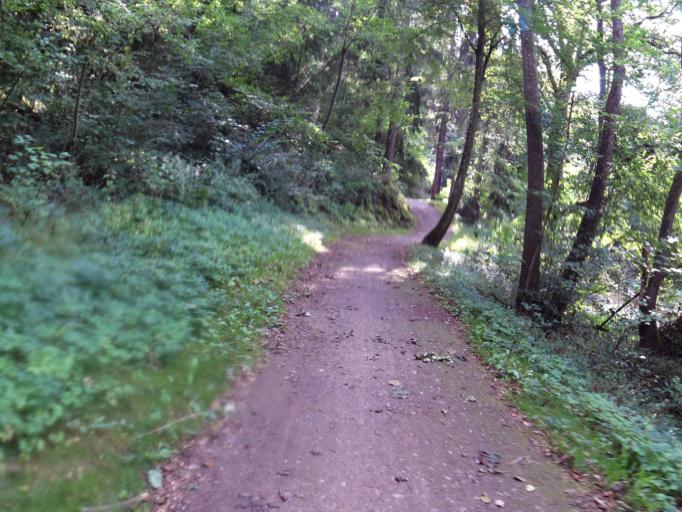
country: DE
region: Rheinland-Pfalz
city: Philippsheim
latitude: 49.9472
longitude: 6.6338
